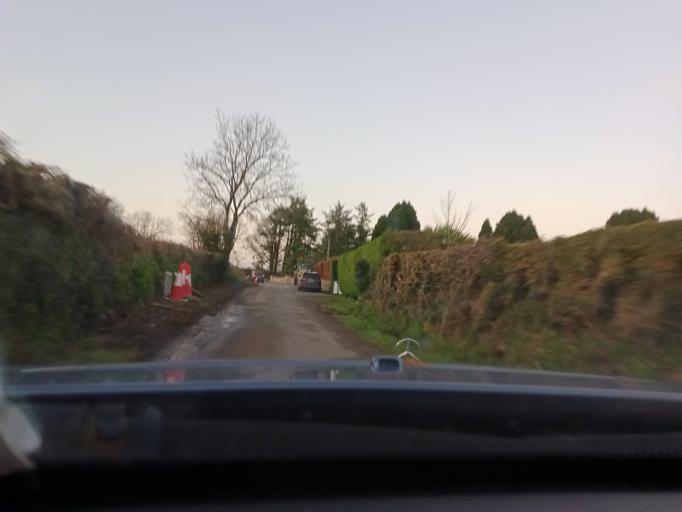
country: IE
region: Munster
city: Carrick-on-Suir
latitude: 52.4435
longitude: -7.3923
